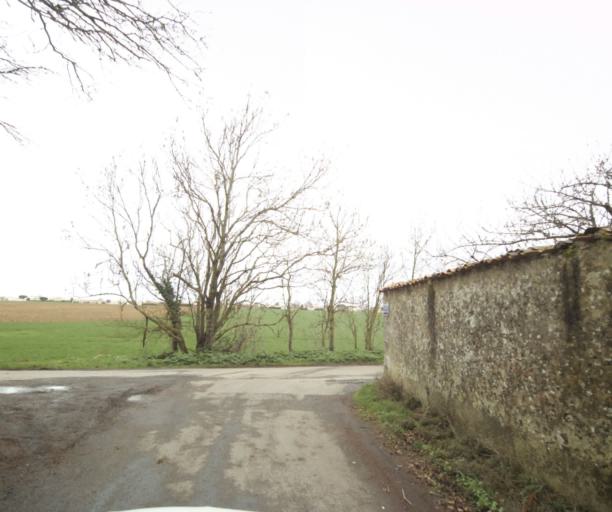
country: FR
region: Poitou-Charentes
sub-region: Departement de la Charente-Maritime
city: Nieul-sur-Mer
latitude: 46.1957
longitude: -1.1690
